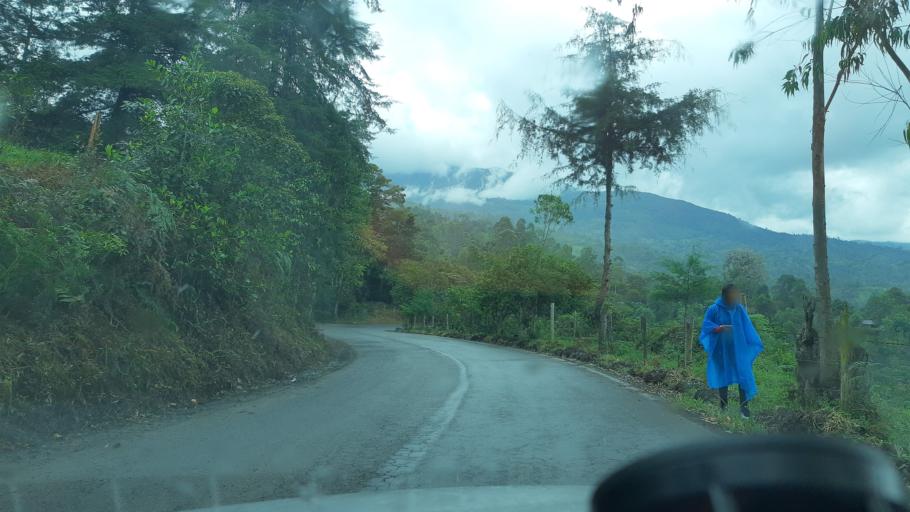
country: CO
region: Boyaca
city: Chinavita
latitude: 5.1527
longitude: -73.3644
